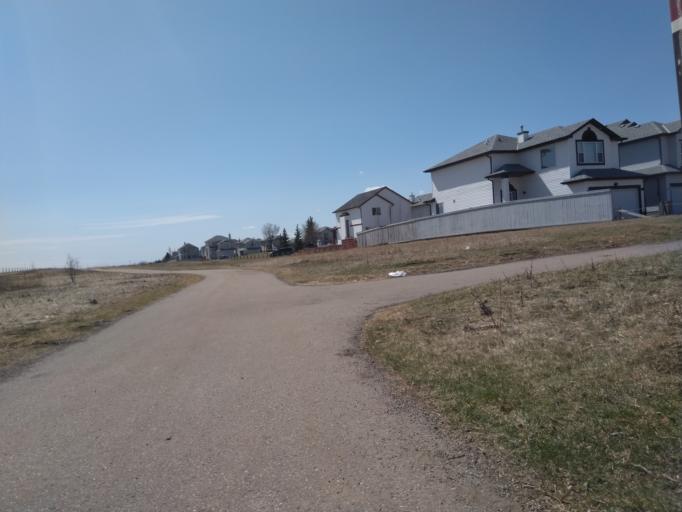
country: CA
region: Alberta
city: Chestermere
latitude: 51.0917
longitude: -113.9243
